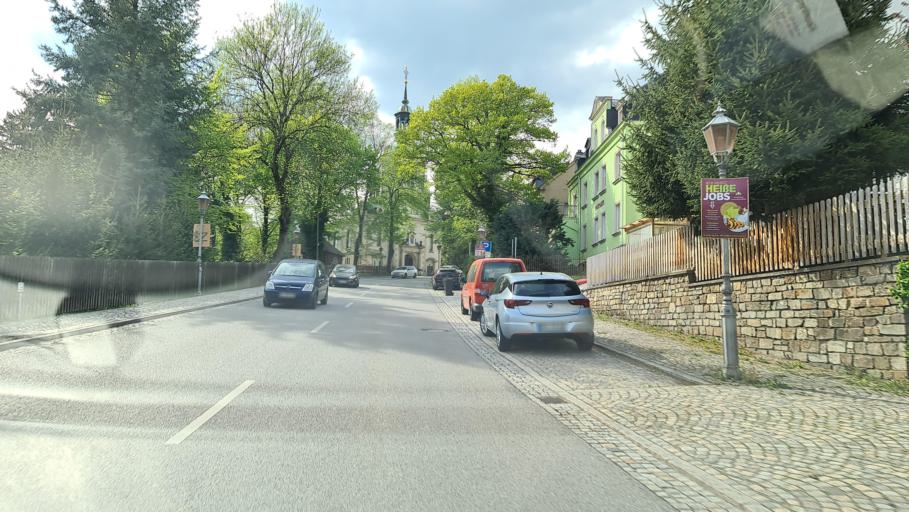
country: DE
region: Saxony
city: Beierfeld
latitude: 50.5611
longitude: 12.7885
